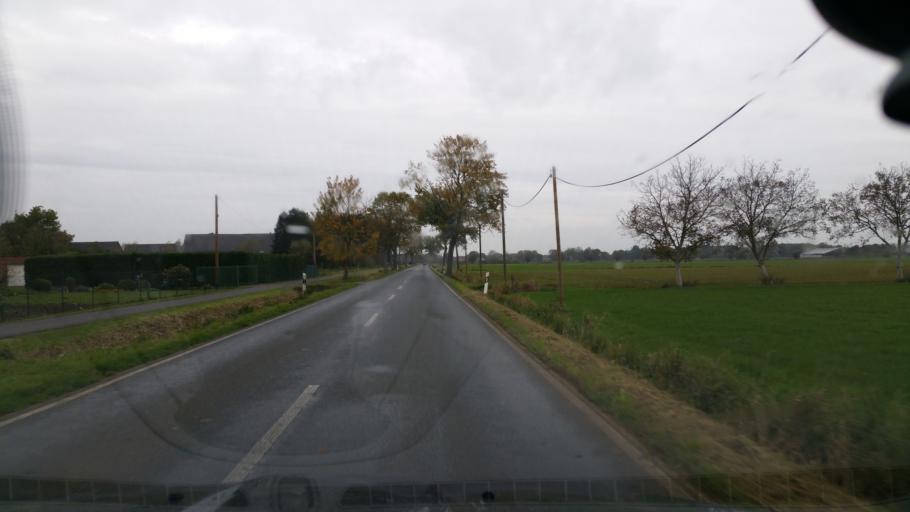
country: DE
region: North Rhine-Westphalia
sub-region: Regierungsbezirk Dusseldorf
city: Mehrhoog
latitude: 51.7831
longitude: 6.5402
